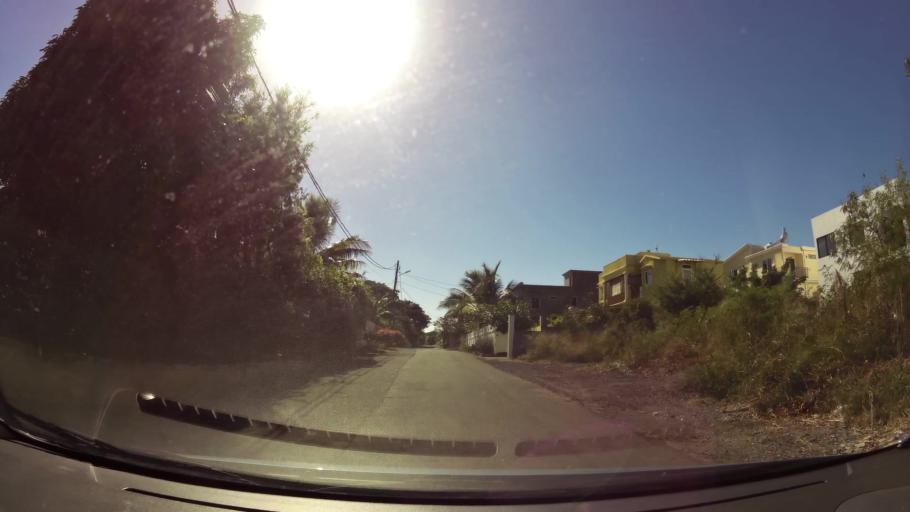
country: MU
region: Black River
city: Flic en Flac
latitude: -20.2638
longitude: 57.3772
